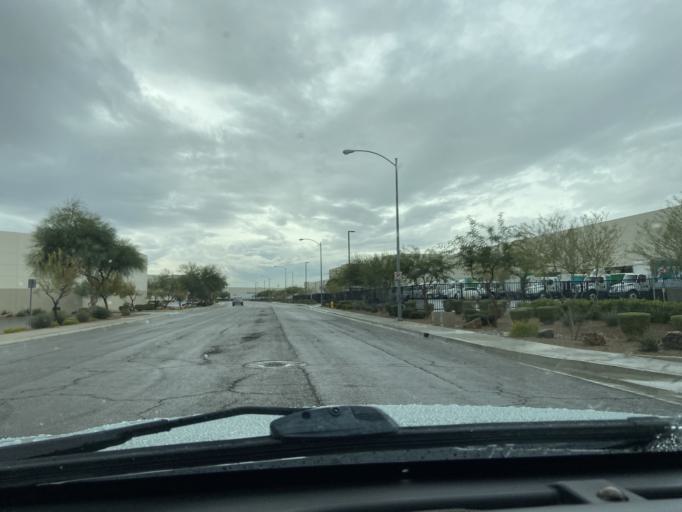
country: US
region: Nevada
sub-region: Clark County
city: Sunrise Manor
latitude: 36.2365
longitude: -115.1036
